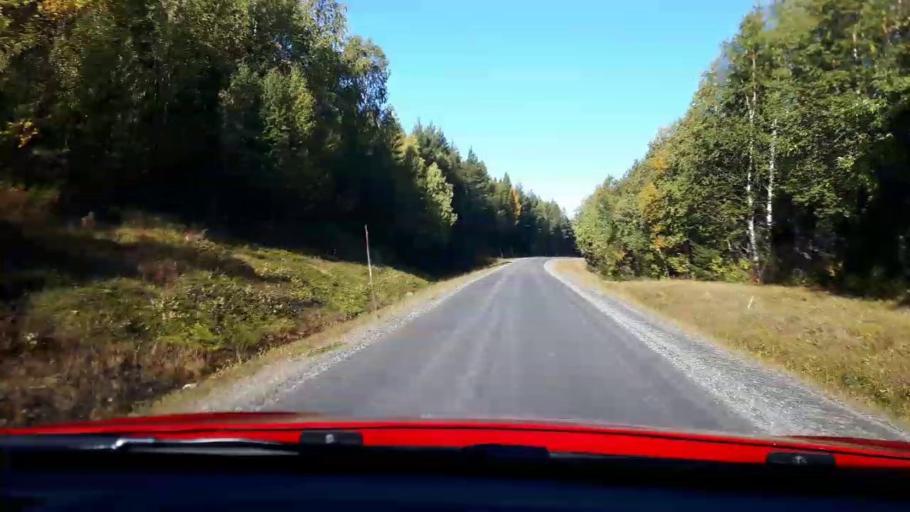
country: NO
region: Nord-Trondelag
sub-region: Lierne
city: Sandvika
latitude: 64.5372
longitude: 14.0123
